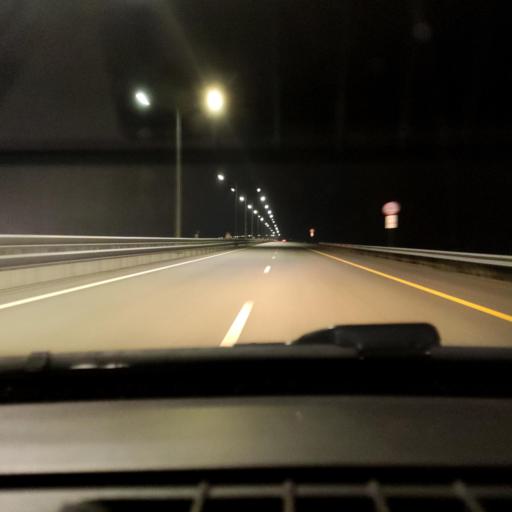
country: RU
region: Voronezj
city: Novaya Usman'
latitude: 51.5974
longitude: 39.3537
